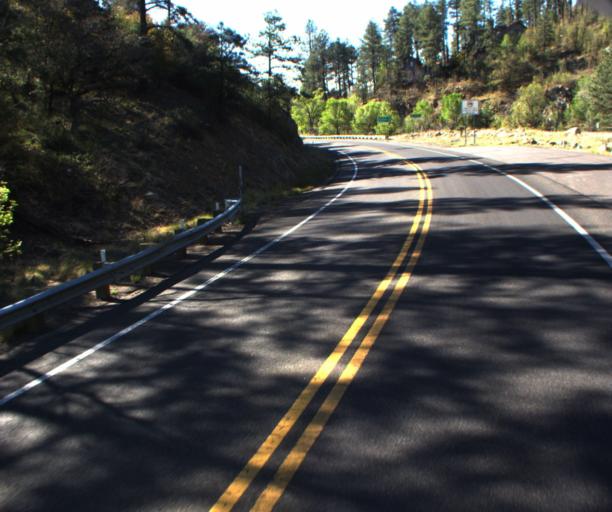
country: US
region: Arizona
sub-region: Yavapai County
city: Prescott
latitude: 34.5194
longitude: -112.4791
